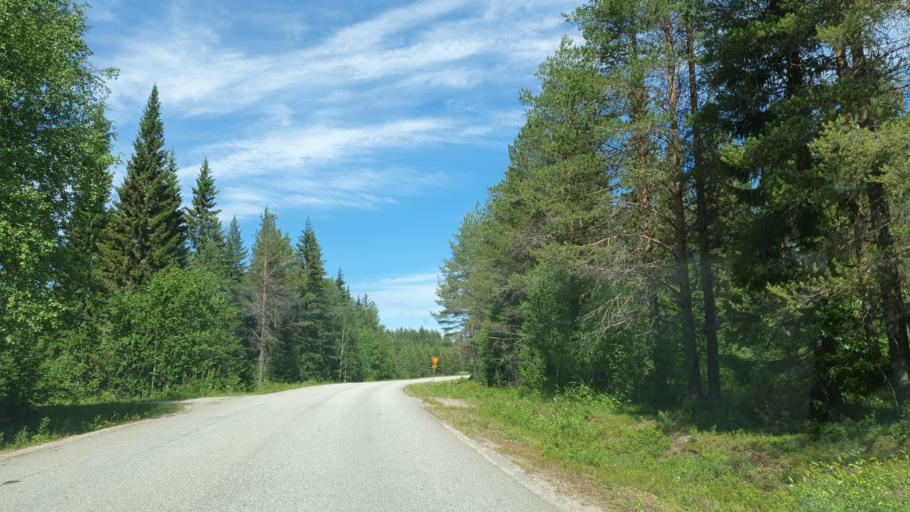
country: FI
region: Kainuu
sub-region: Kehys-Kainuu
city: Suomussalmi
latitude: 64.5925
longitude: 29.1017
